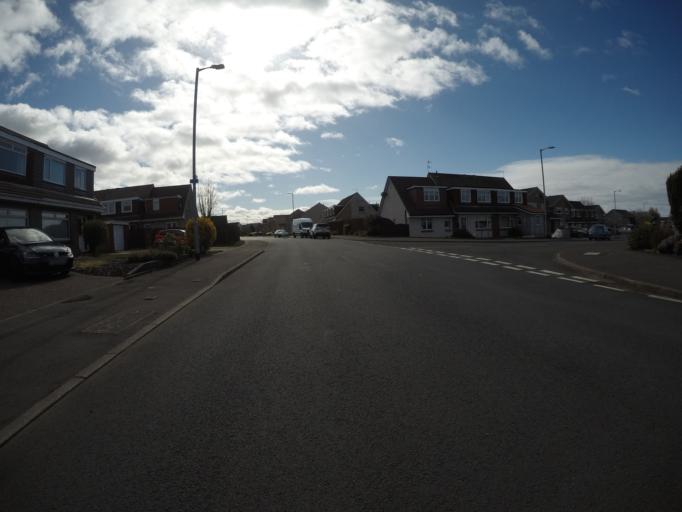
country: GB
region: Scotland
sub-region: South Ayrshire
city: Troon
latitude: 55.5664
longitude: -4.6405
